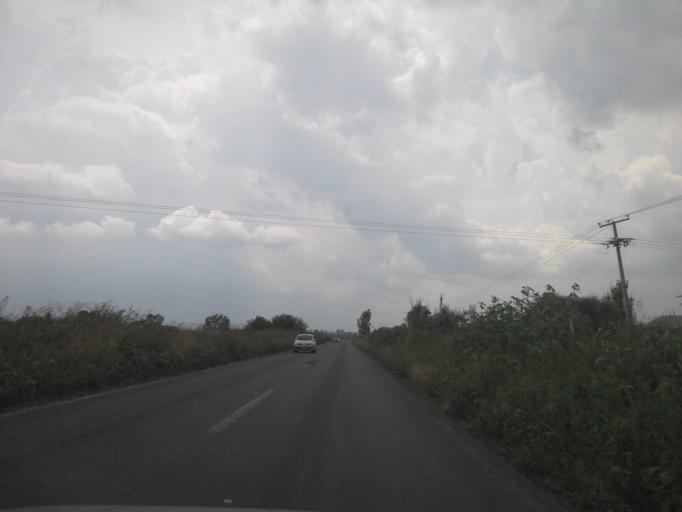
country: MX
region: Guanajuato
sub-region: San Francisco del Rincon
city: San Ignacio de Hidalgo
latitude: 20.8920
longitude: -101.9527
